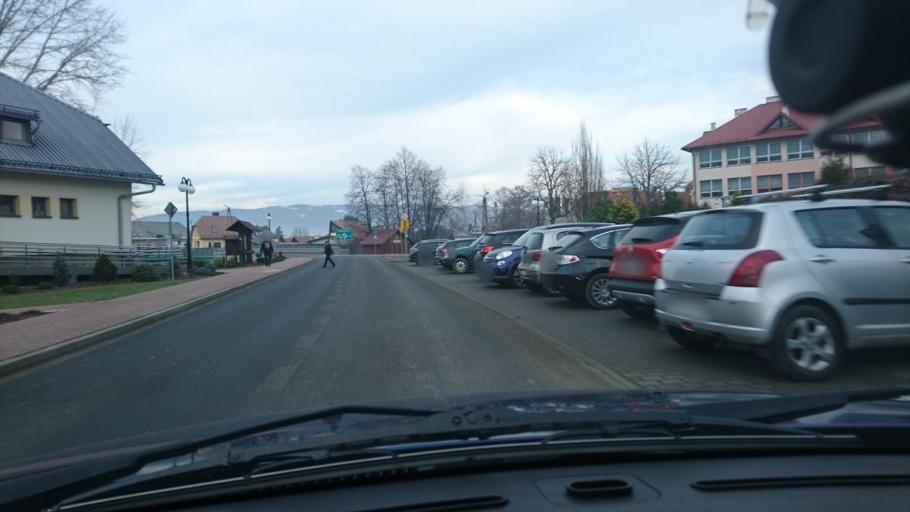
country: PL
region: Silesian Voivodeship
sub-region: Powiat bielski
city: Buczkowice
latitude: 49.7273
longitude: 19.0685
